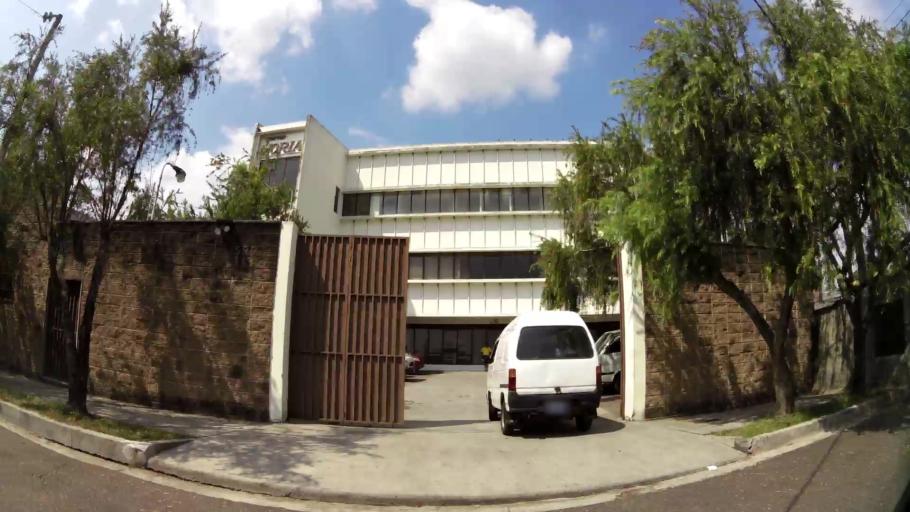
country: SV
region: San Salvador
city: Mejicanos
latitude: 13.7138
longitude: -89.2227
